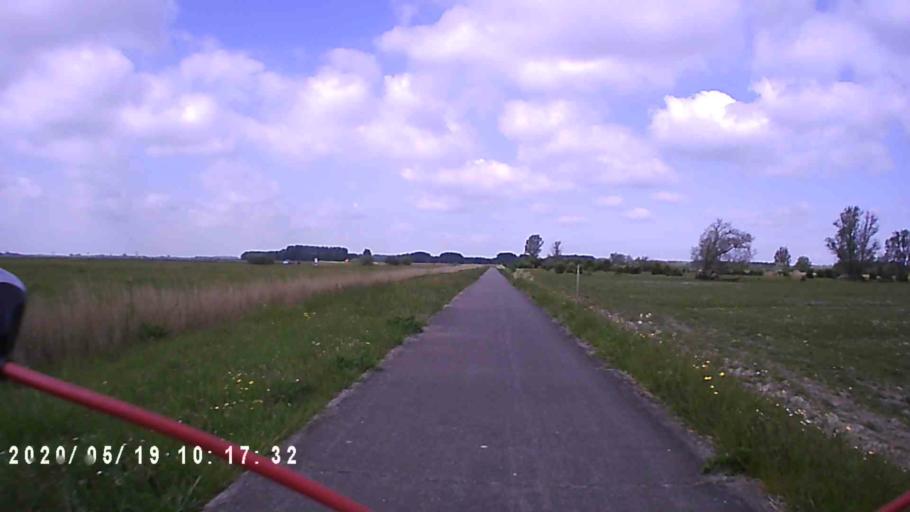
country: NL
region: Friesland
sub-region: Gemeente Kollumerland en Nieuwkruisland
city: Kollum
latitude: 53.3227
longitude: 6.2088
